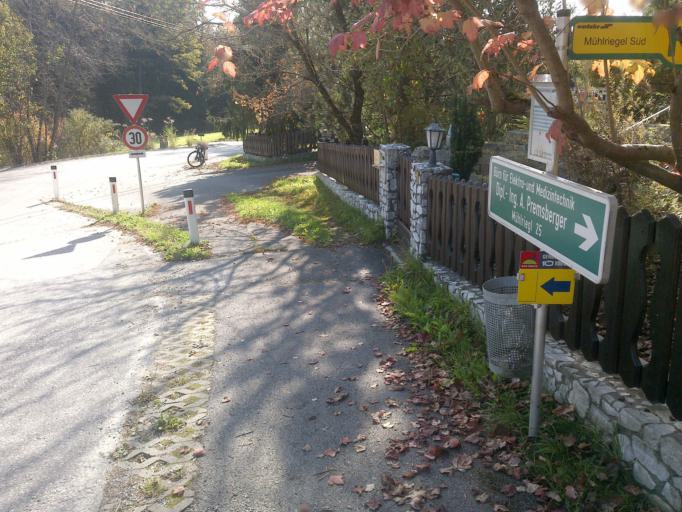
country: AT
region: Styria
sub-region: Politischer Bezirk Graz-Umgebung
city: Pirka
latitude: 47.0129
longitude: 15.3586
